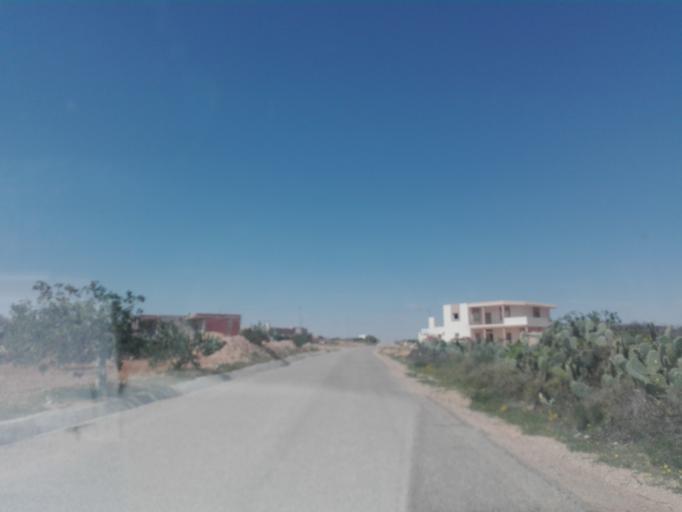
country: TN
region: Safaqis
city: Bi'r `Ali Bin Khalifah
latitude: 34.6688
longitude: 10.3548
